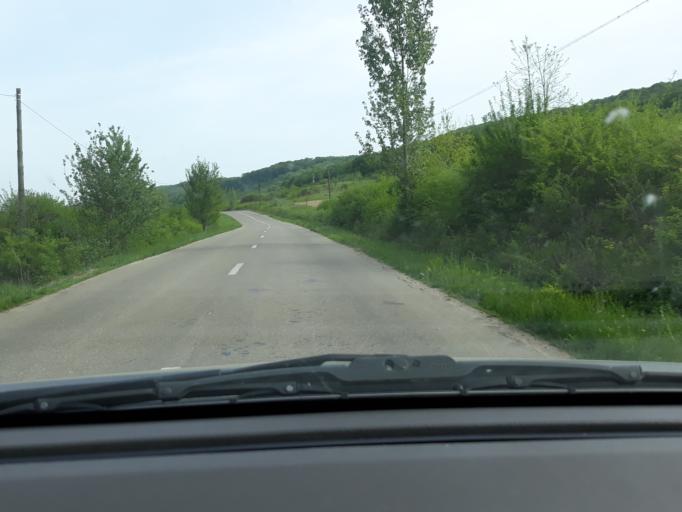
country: RO
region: Bihor
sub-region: Comuna Sanmartin
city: Sanmartin
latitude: 46.9794
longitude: 22.0017
